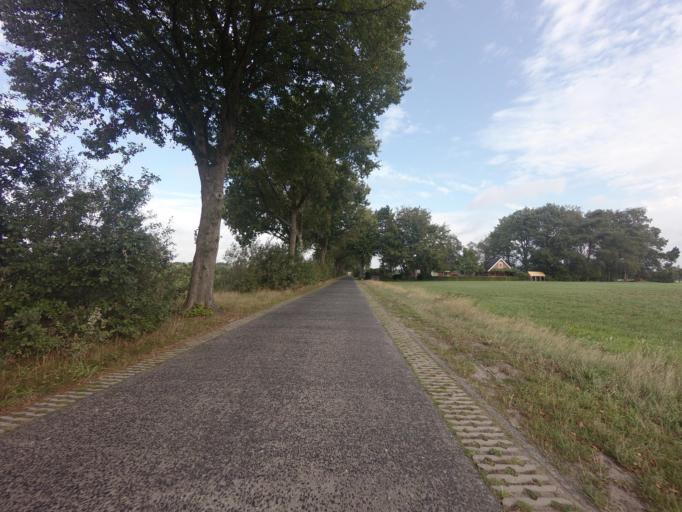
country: NL
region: Friesland
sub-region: Gemeente Heerenveen
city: Jubbega
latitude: 52.9805
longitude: 6.1461
